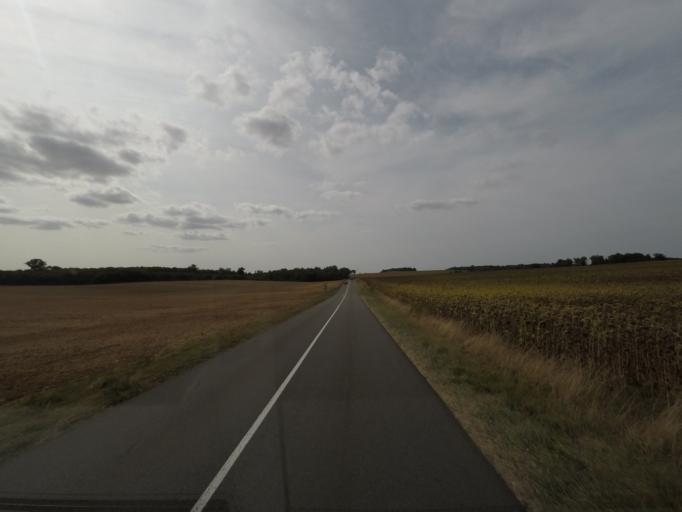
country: FR
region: Poitou-Charentes
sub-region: Departement de la Charente
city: Nanteuil-en-Vallee
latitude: 46.0191
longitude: 0.2725
